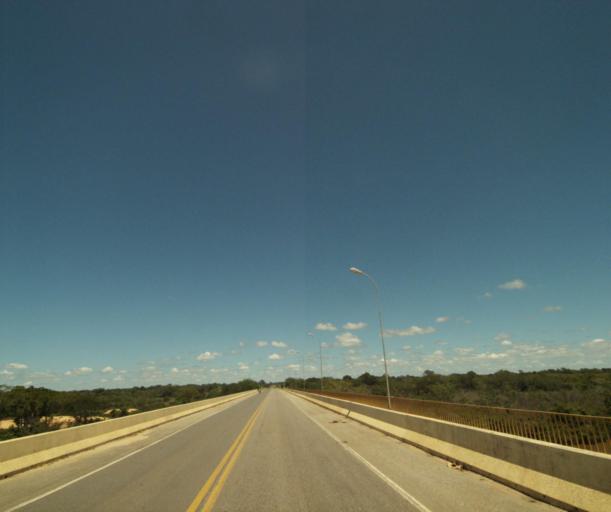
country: BR
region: Bahia
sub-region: Carinhanha
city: Carinhanha
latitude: -14.3229
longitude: -43.7734
